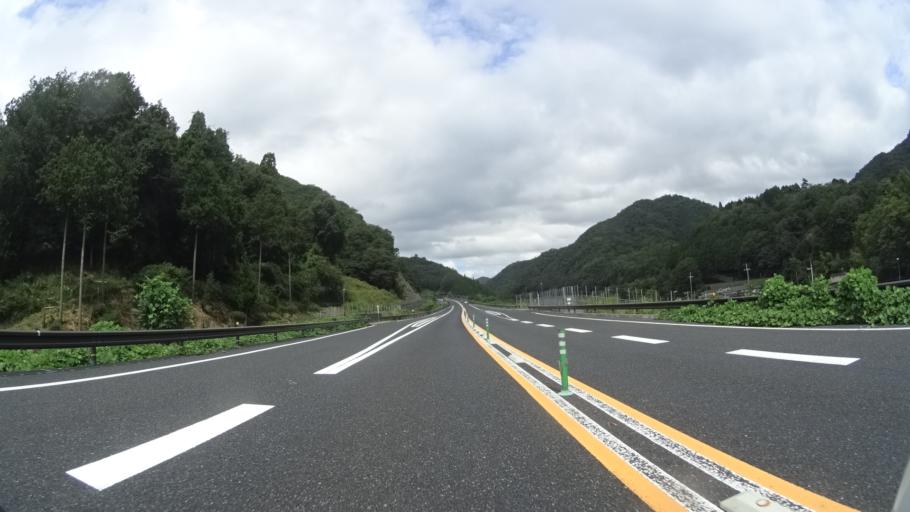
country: JP
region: Hyogo
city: Yamazakicho-nakabirose
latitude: 35.0579
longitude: 134.3657
